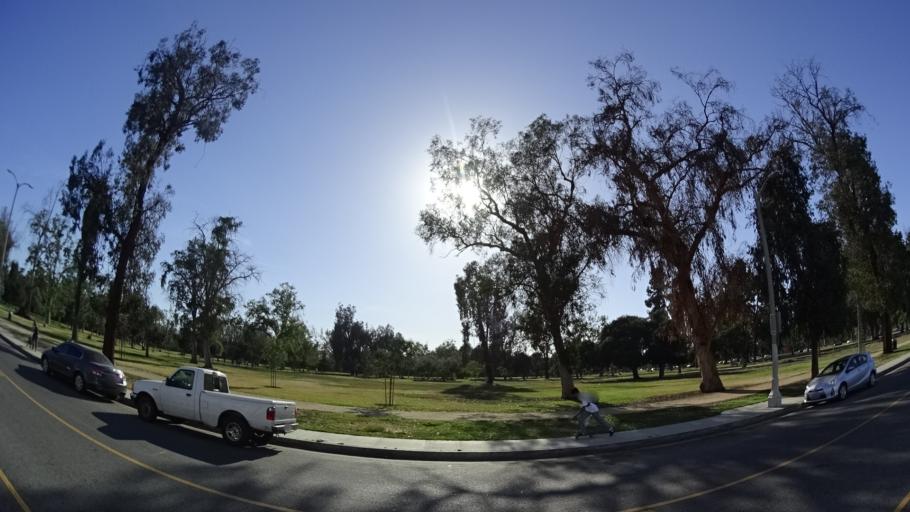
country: US
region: California
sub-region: Los Angeles County
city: North Hollywood
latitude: 34.1634
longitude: -118.3790
